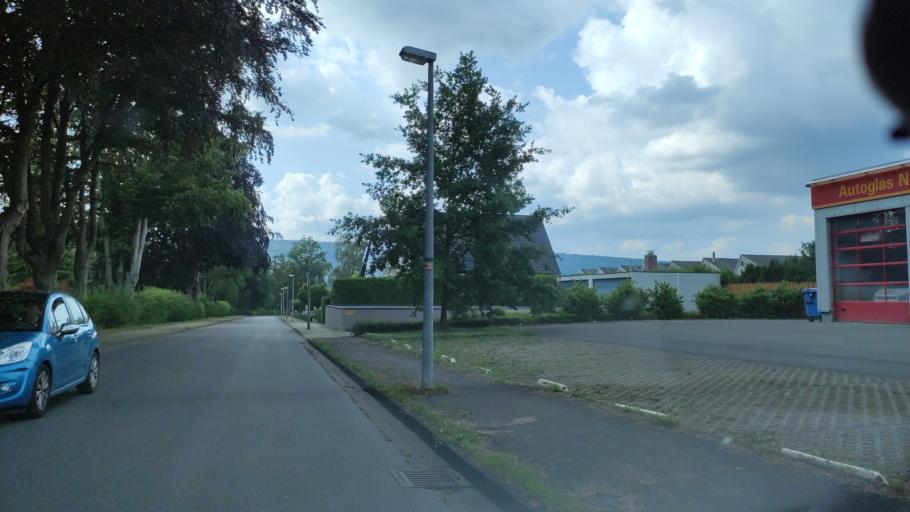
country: DE
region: Lower Saxony
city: Holzminden
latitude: 51.8363
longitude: 9.4625
